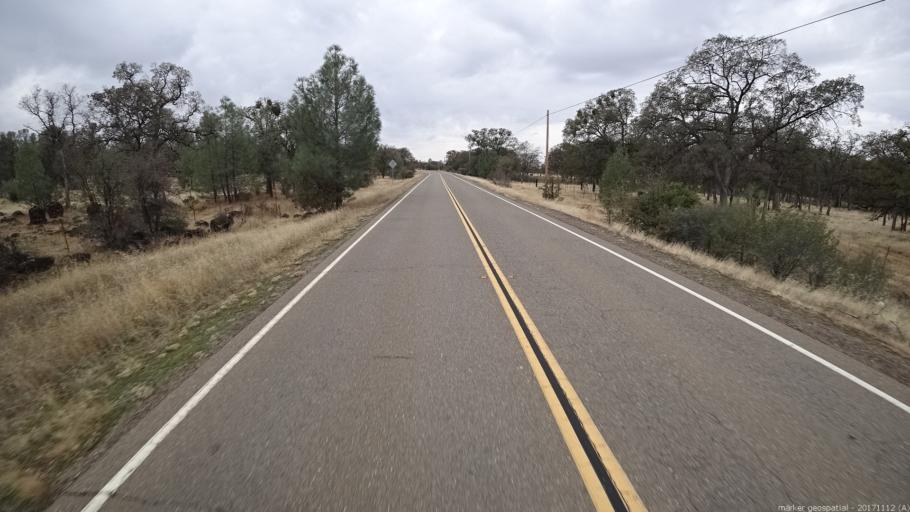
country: US
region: California
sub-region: Shasta County
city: Palo Cedro
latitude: 40.4867
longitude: -122.0755
